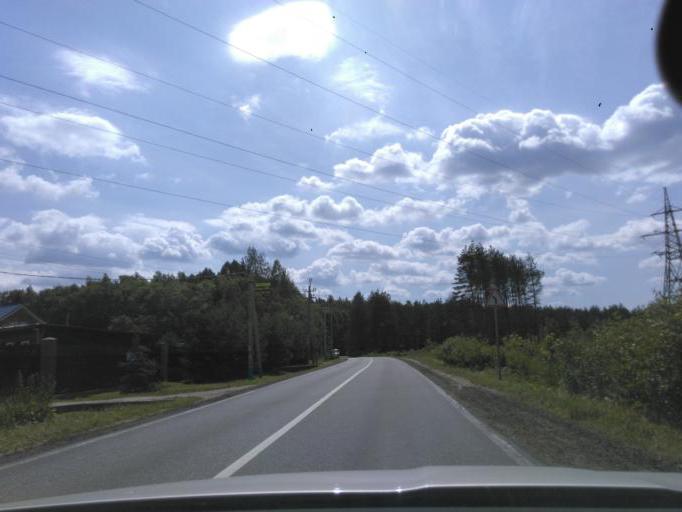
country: RU
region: Moskovskaya
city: Solnechnogorsk
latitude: 56.1577
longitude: 36.9805
